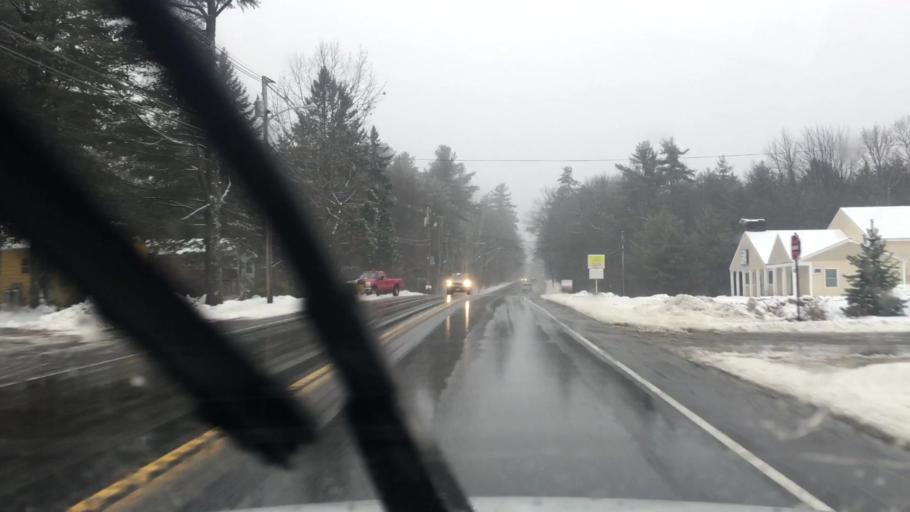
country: US
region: Maine
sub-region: York County
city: Buxton
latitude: 43.7141
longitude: -70.5182
